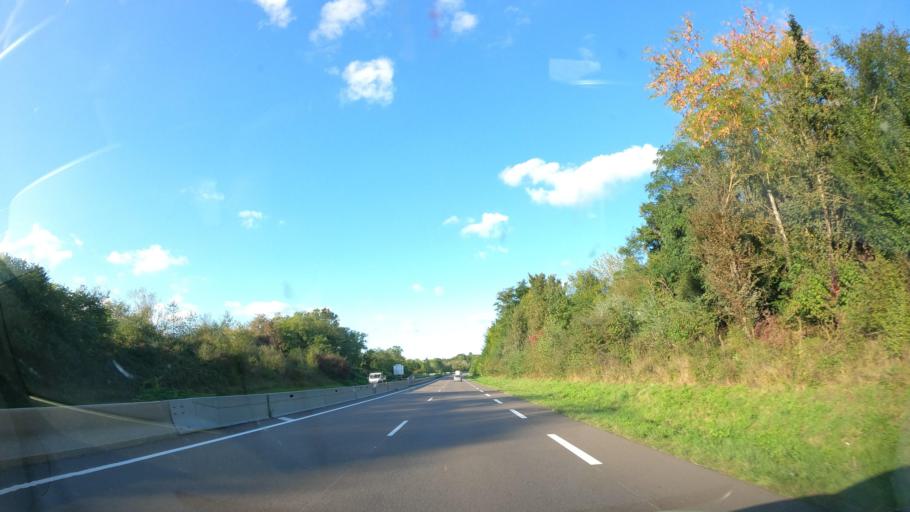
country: FR
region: Bourgogne
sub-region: Departement de Saone-et-Loire
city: Montceau-les-Mines
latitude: 46.6756
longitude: 4.3455
